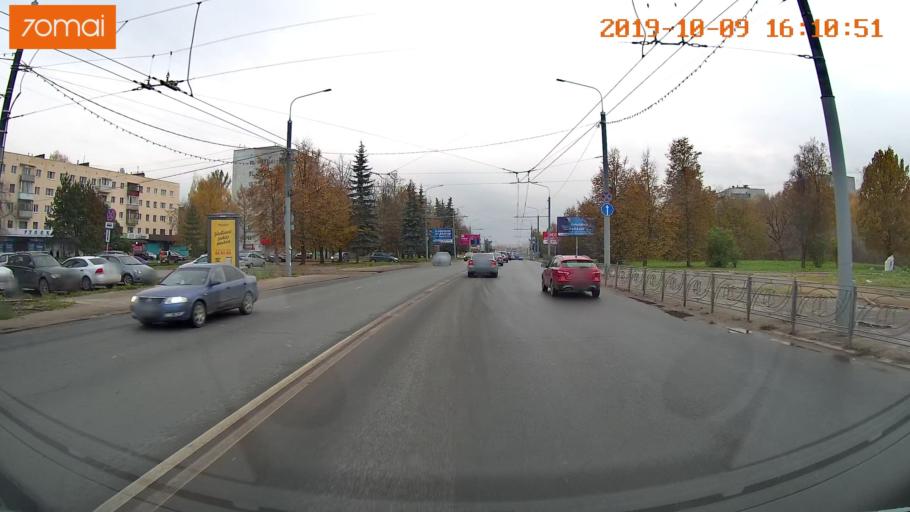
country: RU
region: Kostroma
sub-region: Kostromskoy Rayon
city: Kostroma
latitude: 57.7604
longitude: 40.9504
